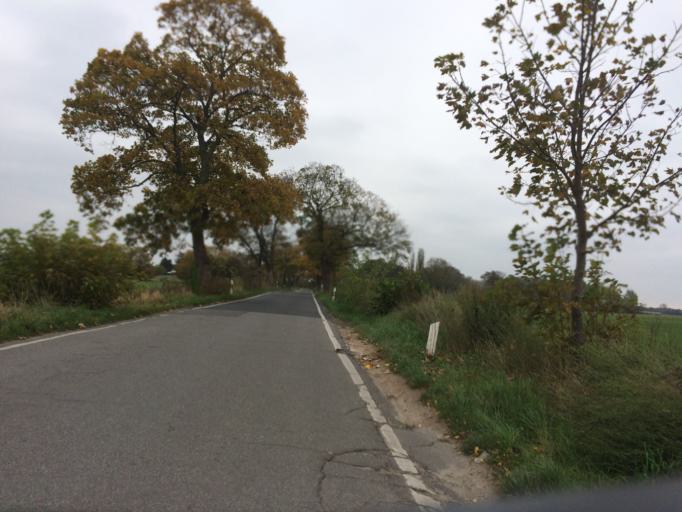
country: DE
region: Berlin
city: Blankenfelde
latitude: 52.6158
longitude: 13.4009
